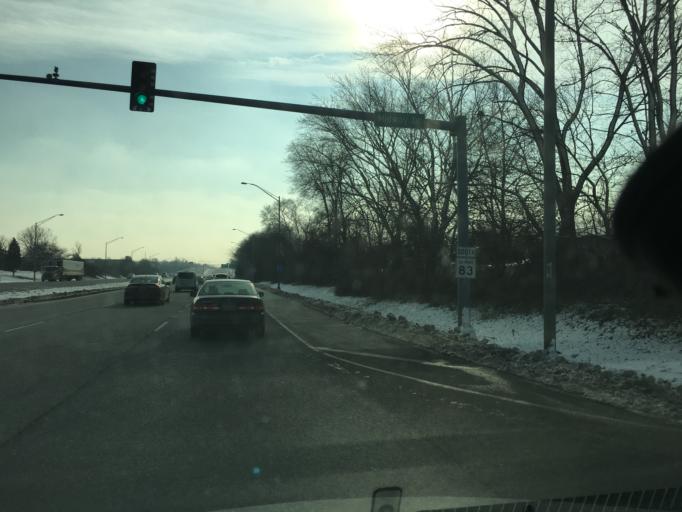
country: US
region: Illinois
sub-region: DuPage County
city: Willowbrook
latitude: 41.7486
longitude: -87.9448
